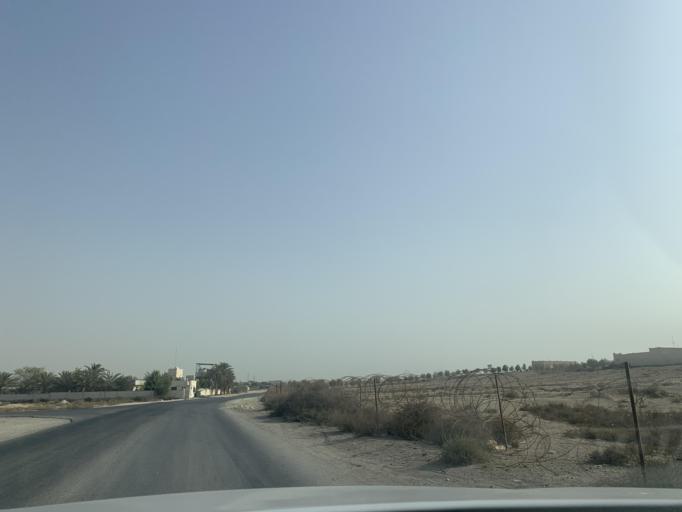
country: BH
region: Central Governorate
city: Madinat Hamad
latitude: 26.1593
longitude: 50.4884
